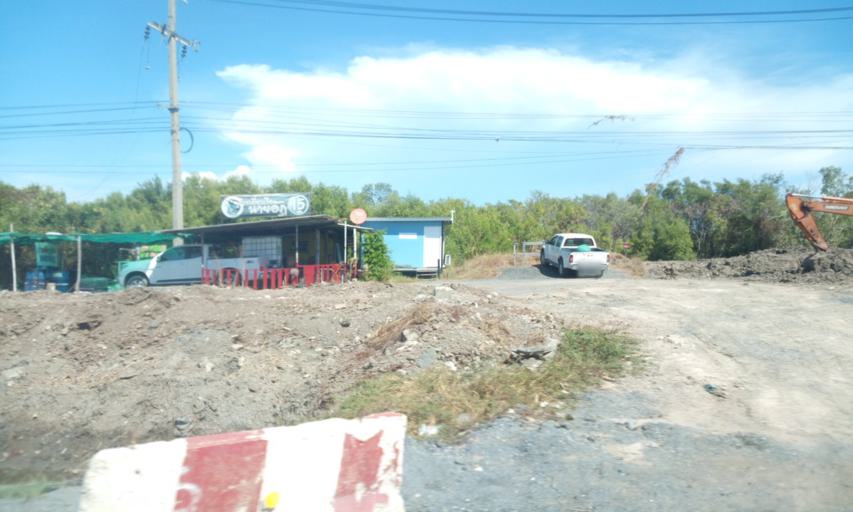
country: TH
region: Samut Prakan
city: Bang Bo District
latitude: 13.5047
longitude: 100.7779
